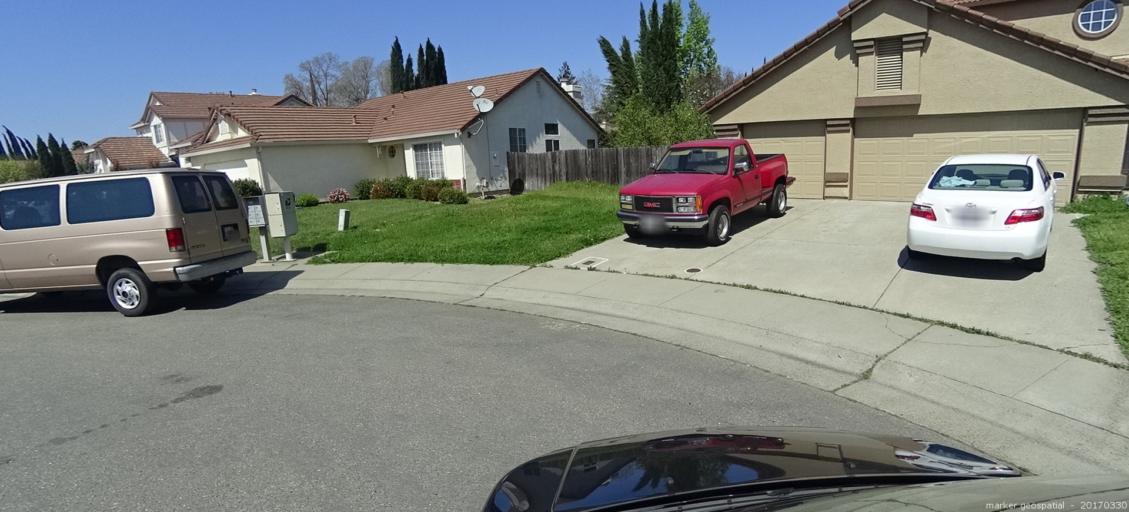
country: US
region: California
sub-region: Sacramento County
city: Florin
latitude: 38.4602
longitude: -121.4227
